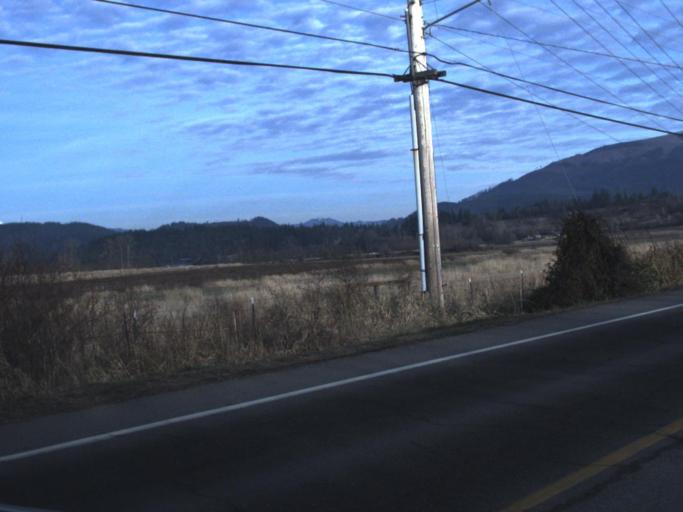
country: US
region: Washington
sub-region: Skagit County
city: Mount Vernon
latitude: 48.4355
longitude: -122.2836
